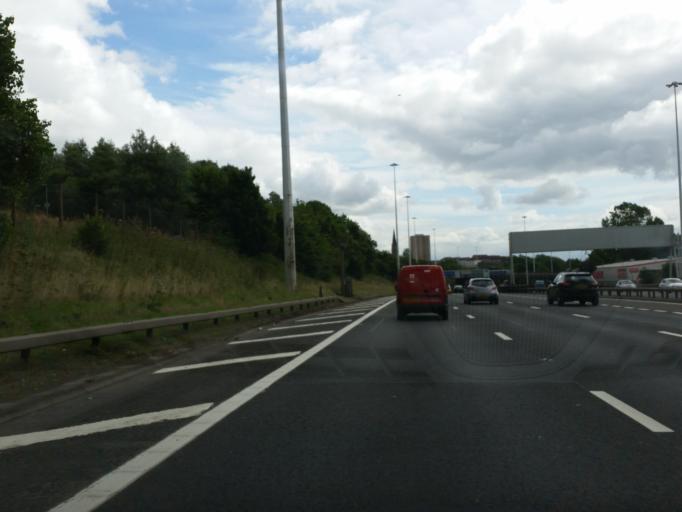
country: GB
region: Scotland
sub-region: Glasgow City
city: Glasgow
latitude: 55.8696
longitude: -4.2439
